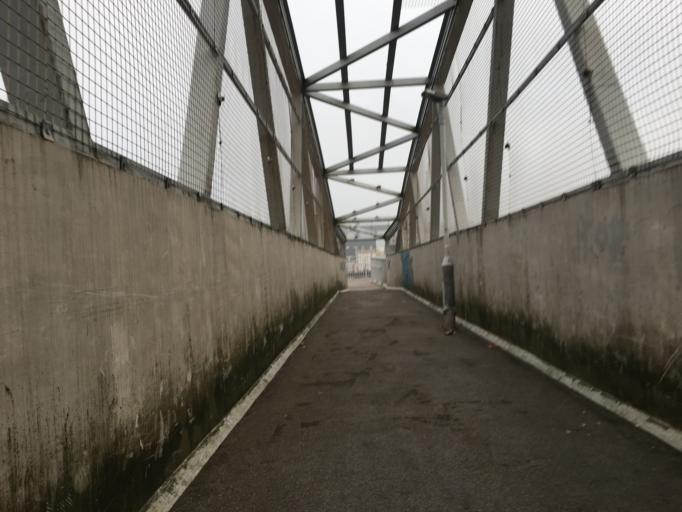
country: GB
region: England
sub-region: Warwickshire
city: Rugby
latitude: 52.3809
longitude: -1.2578
